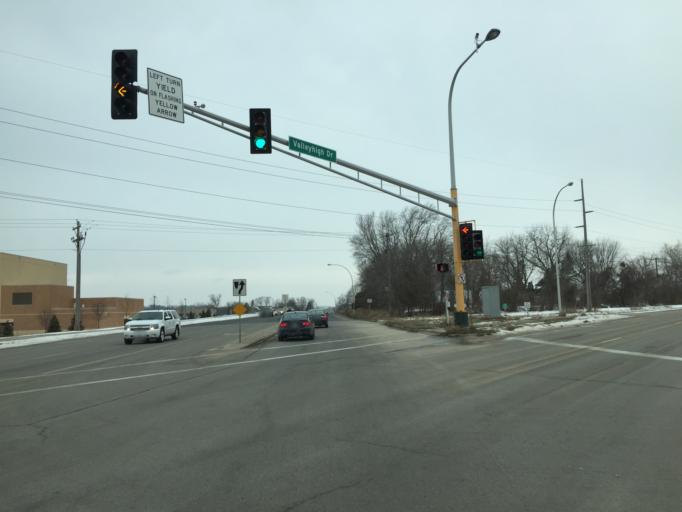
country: US
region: Minnesota
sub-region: Olmsted County
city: Rochester
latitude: 44.0436
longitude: -92.5023
